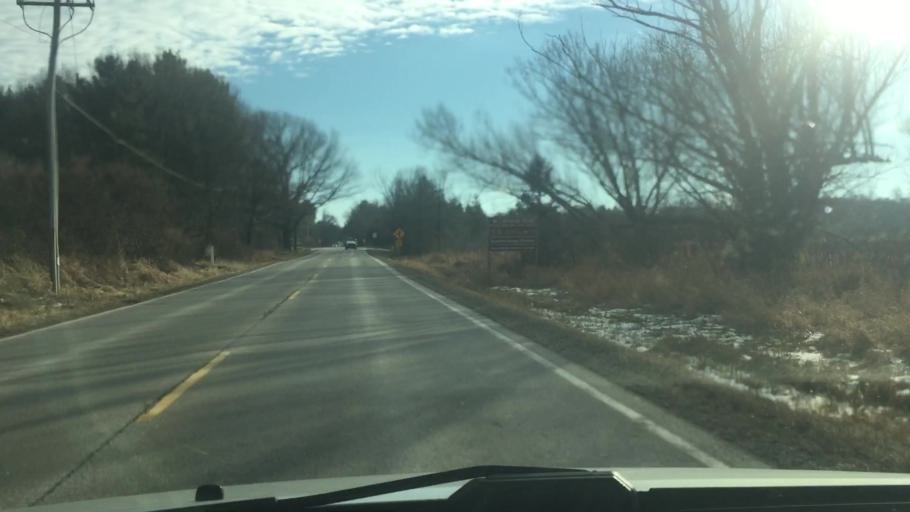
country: US
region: Wisconsin
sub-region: Waukesha County
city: Delafield
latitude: 43.0431
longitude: -88.4043
